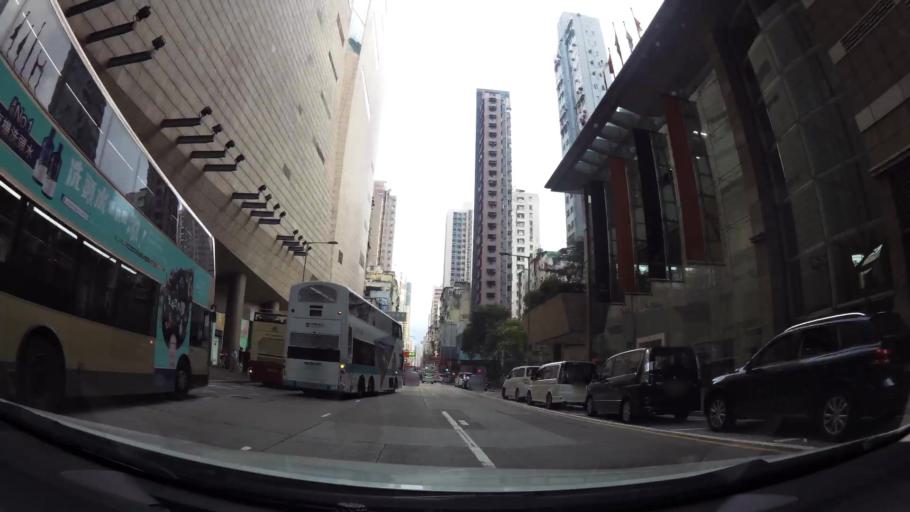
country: HK
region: Sham Shui Po
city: Sham Shui Po
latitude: 22.3181
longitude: 114.1683
